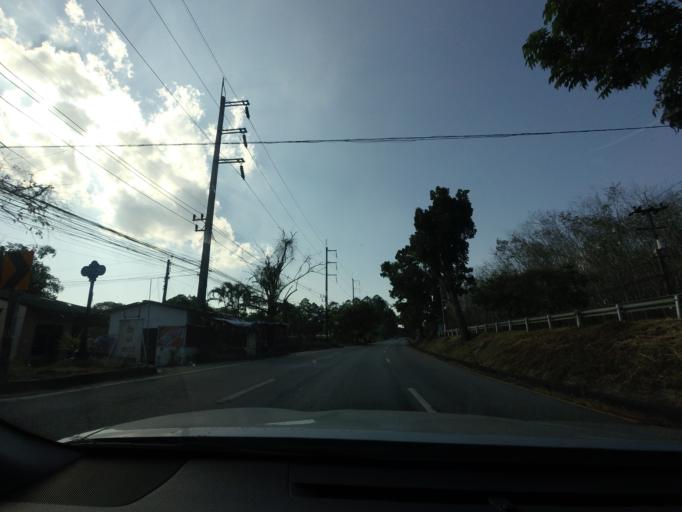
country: TH
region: Phangnga
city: Thai Mueang
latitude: 8.2706
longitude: 98.3178
